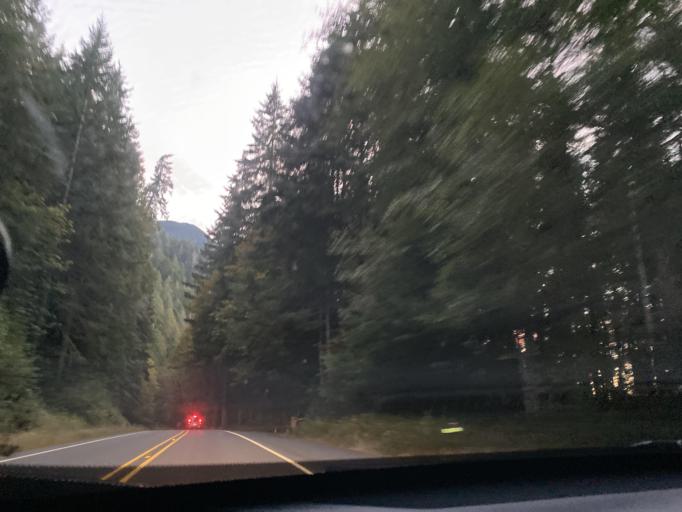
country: CA
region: British Columbia
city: Sooke
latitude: 48.0505
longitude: -123.8014
